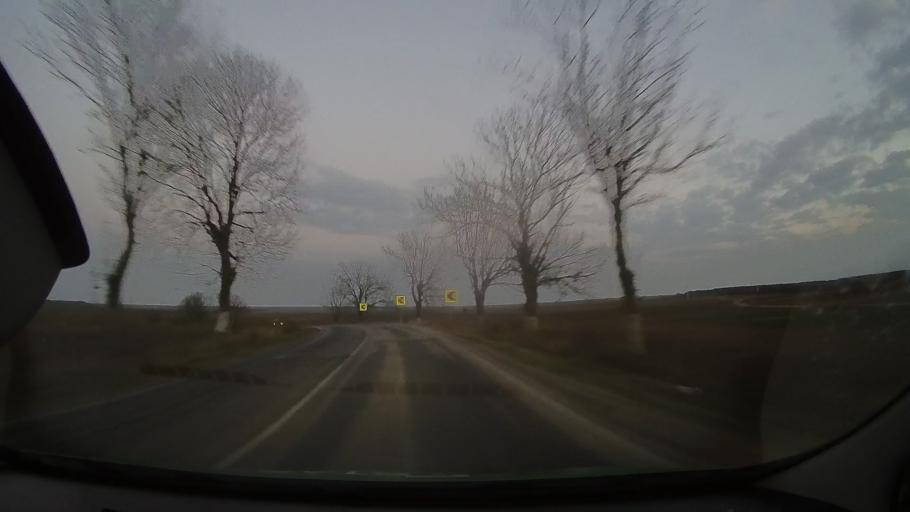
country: RO
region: Constanta
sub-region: Comuna Baneasa
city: Baneasa
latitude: 44.0685
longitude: 27.7306
